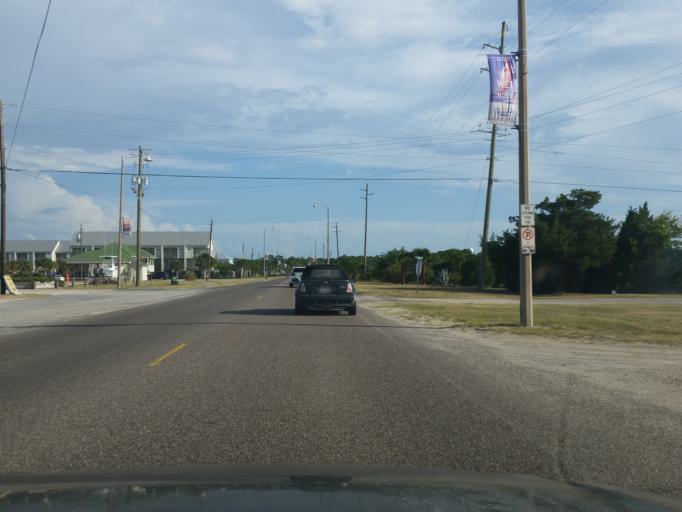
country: US
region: Alabama
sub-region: Mobile County
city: Dauphin Island
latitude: 30.2636
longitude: -88.1150
